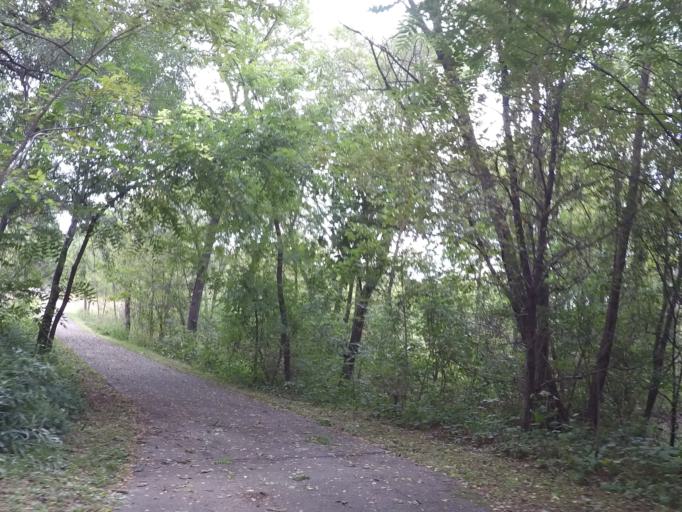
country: US
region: Wisconsin
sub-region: Sauk County
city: Sauk City
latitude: 43.2765
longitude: -89.7198
